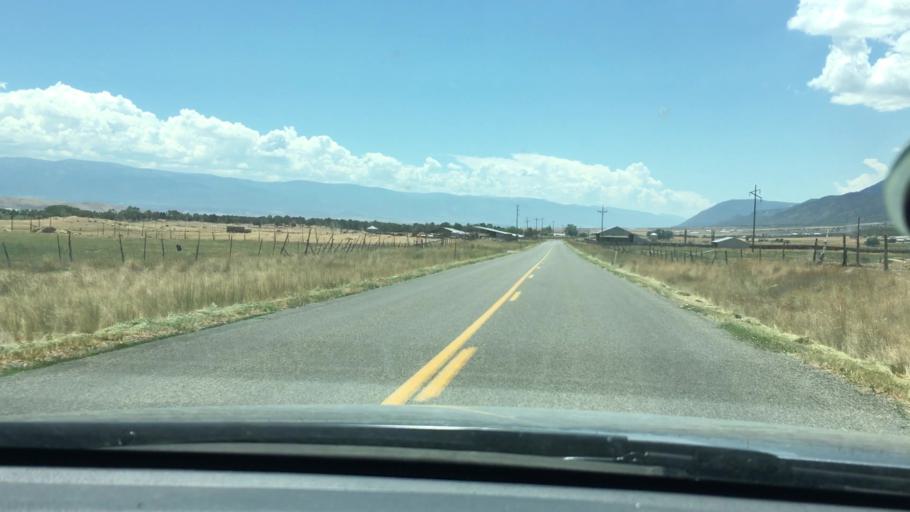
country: US
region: Utah
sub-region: Sanpete County
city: Fountain Green
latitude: 39.6125
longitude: -111.6448
